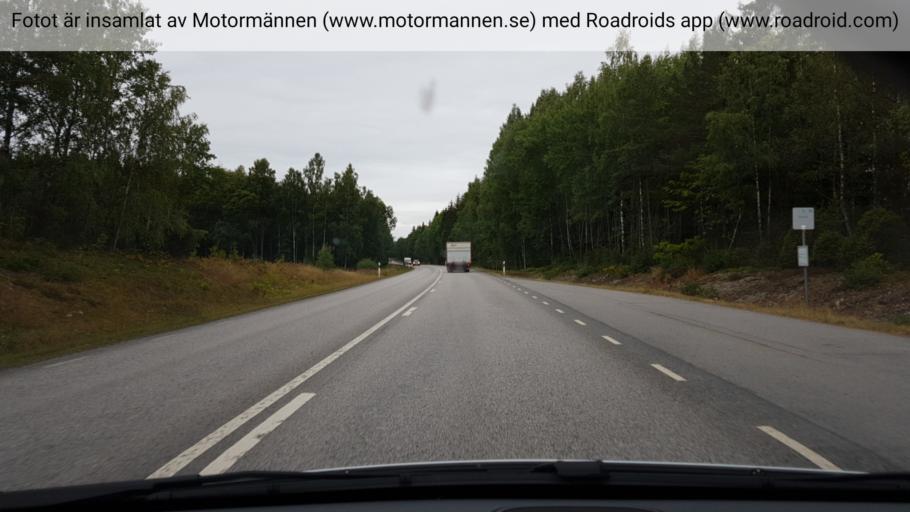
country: SE
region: Vaestra Goetaland
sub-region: Karlsborgs Kommun
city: Molltorp
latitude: 58.4879
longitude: 14.3601
